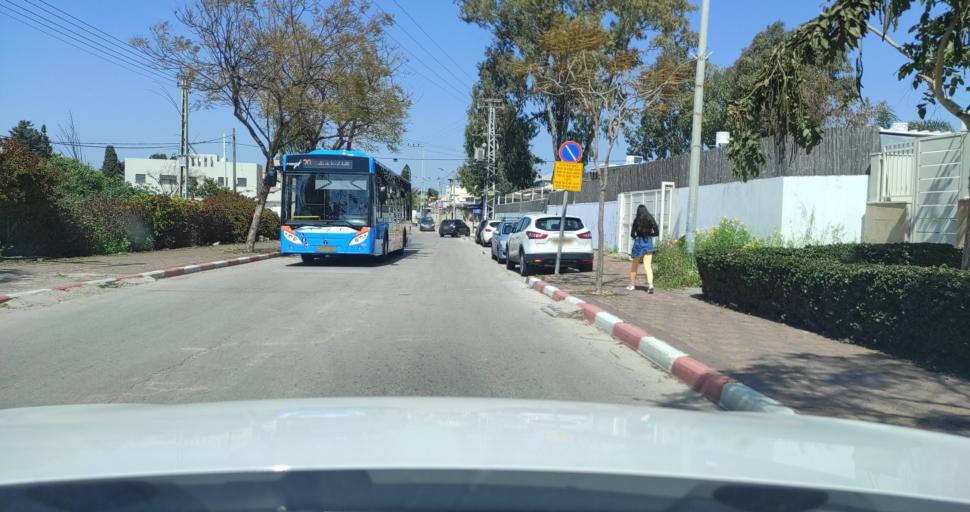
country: IL
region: Central District
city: Nordiyya
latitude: 32.3099
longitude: 34.8815
